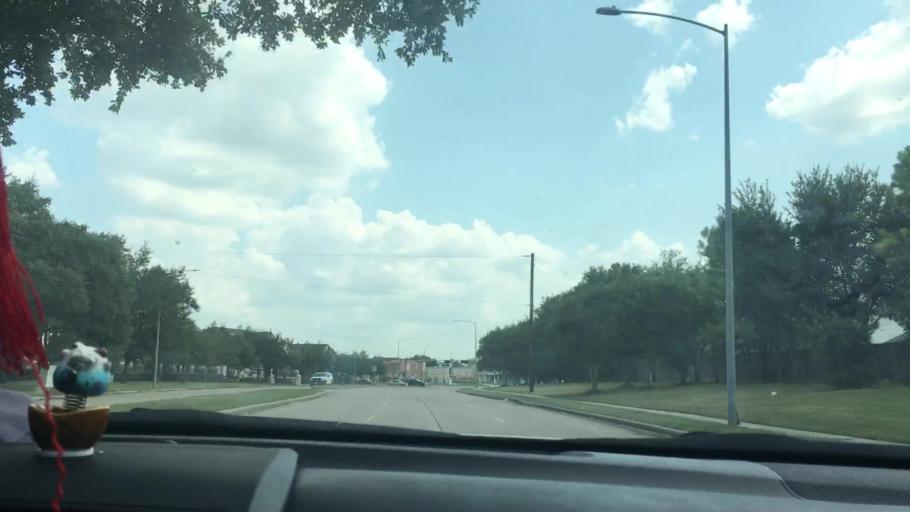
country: US
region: Texas
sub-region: Fort Bend County
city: Mission Bend
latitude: 29.7311
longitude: -95.6365
